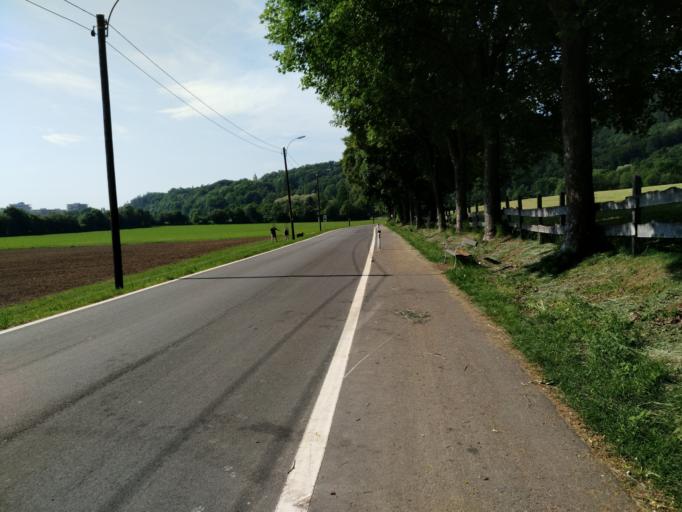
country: AT
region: Styria
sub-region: Graz Stadt
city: Wetzelsdorf
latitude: 47.0453
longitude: 15.3864
